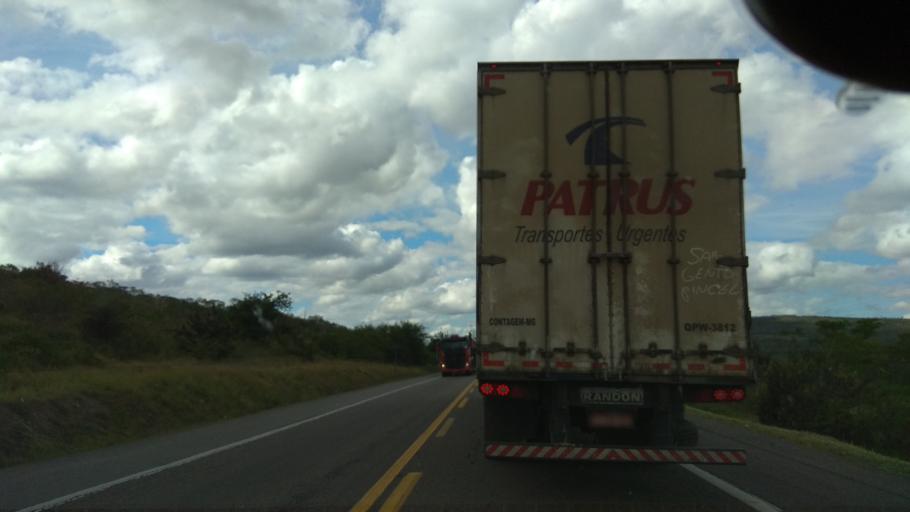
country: BR
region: Bahia
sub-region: Santa Ines
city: Santa Ines
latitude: -12.9927
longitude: -39.9503
